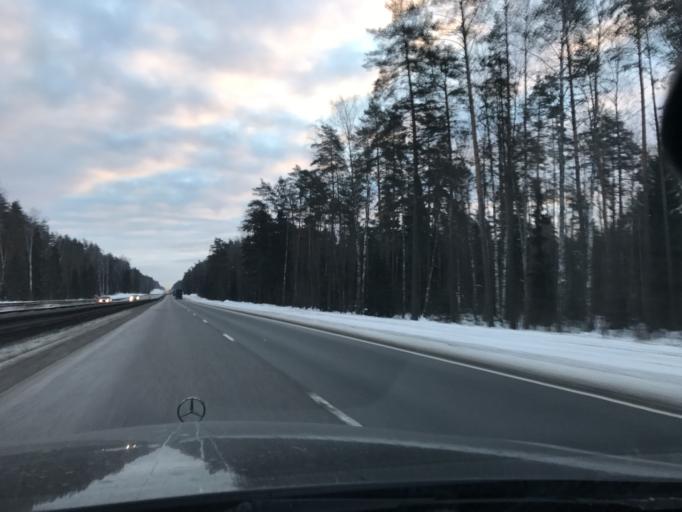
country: RU
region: Vladimir
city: Stepantsevo
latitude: 56.2227
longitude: 41.5569
